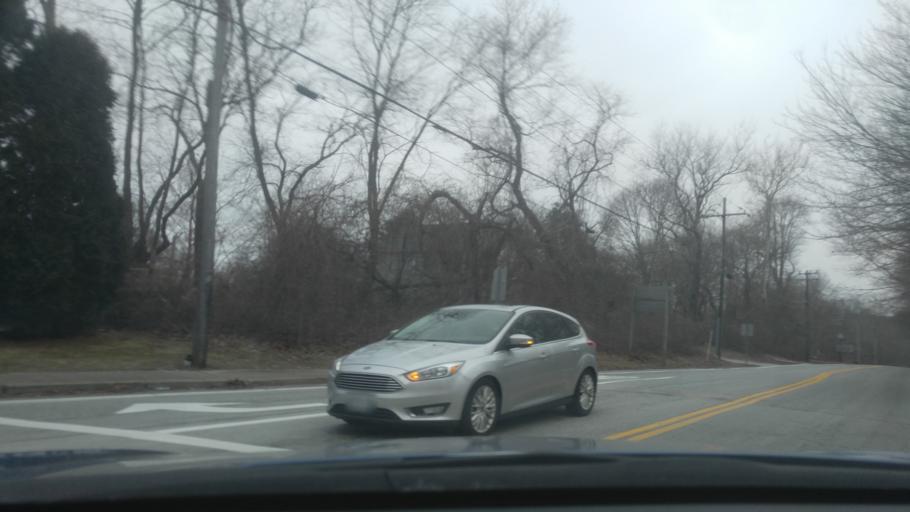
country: US
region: Rhode Island
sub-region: Washington County
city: Narragansett Pier
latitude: 41.4921
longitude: -71.4381
